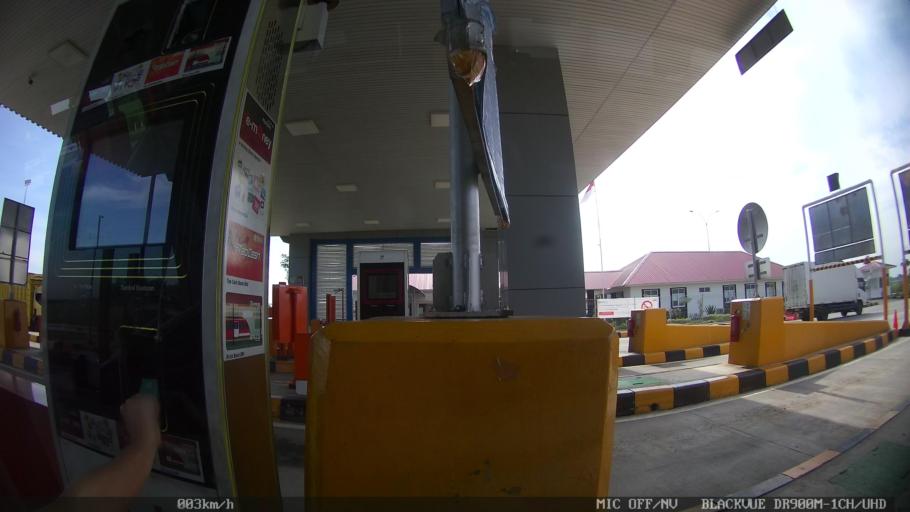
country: ID
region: North Sumatra
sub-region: Kabupaten Langkat
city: Stabat
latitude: 3.7194
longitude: 98.4936
